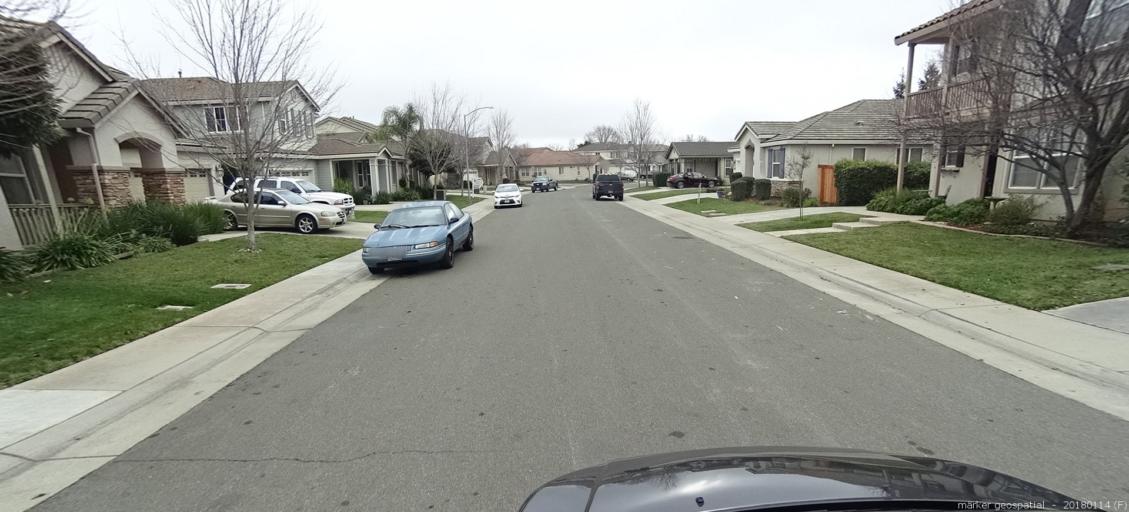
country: US
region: California
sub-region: Sacramento County
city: Gold River
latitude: 38.5556
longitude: -121.2352
